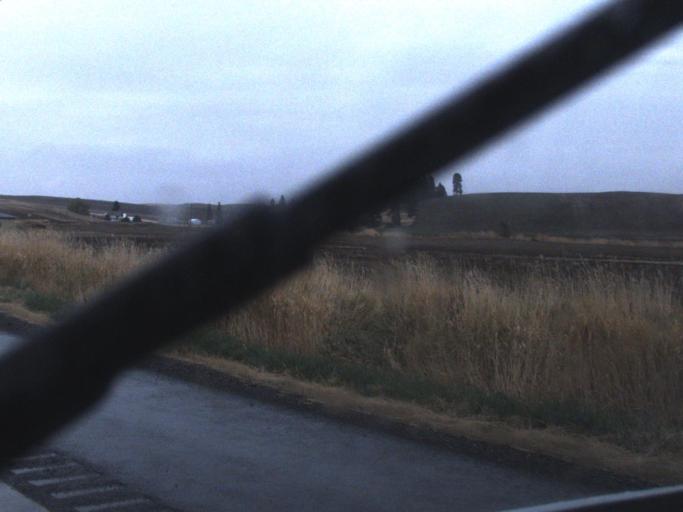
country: US
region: Washington
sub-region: Whitman County
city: Colfax
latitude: 46.9656
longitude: -117.3246
